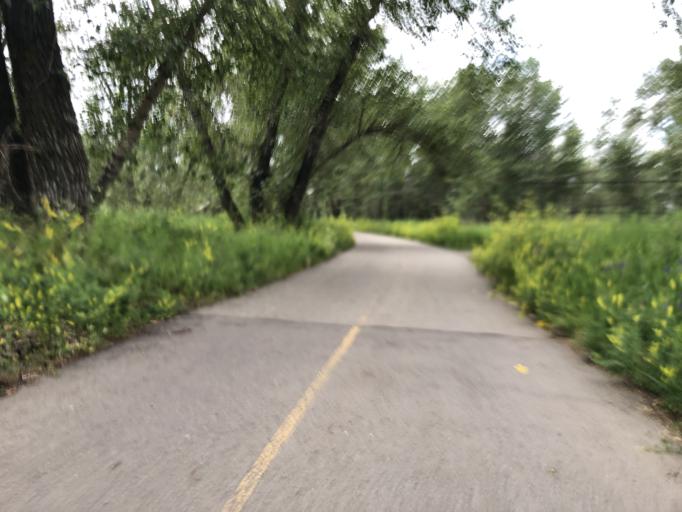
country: CA
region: Alberta
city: Calgary
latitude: 51.0013
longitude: -114.0231
